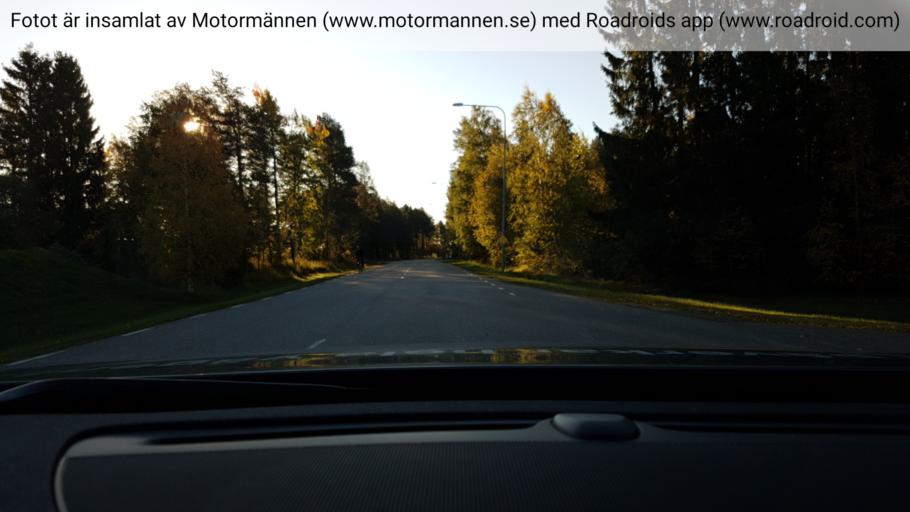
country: SE
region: Norrbotten
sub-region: Lulea Kommun
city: Sodra Sunderbyn
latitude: 65.6532
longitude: 21.9491
